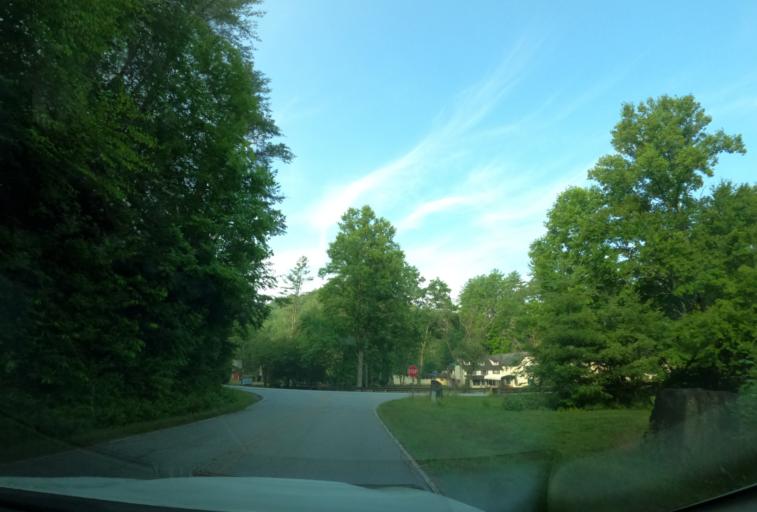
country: US
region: North Carolina
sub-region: Transylvania County
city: Brevard
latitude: 35.2246
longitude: -82.8608
